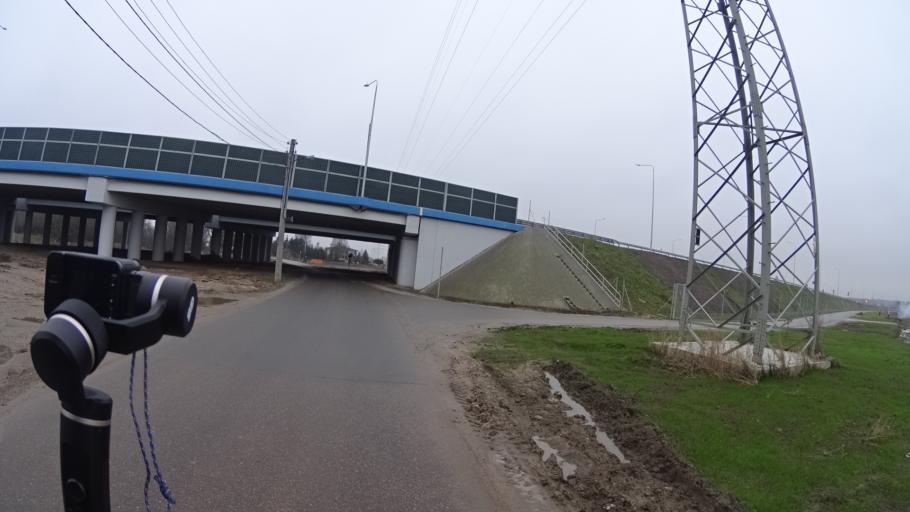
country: PL
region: Masovian Voivodeship
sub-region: Warszawa
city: Wilanow
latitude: 52.1529
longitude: 21.1119
